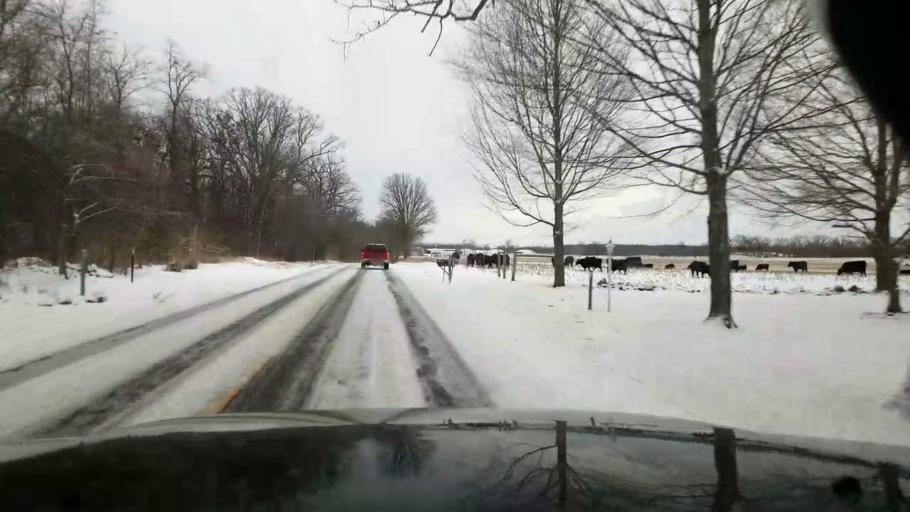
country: US
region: Michigan
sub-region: Jackson County
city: Spring Arbor
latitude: 42.1750
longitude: -84.5006
